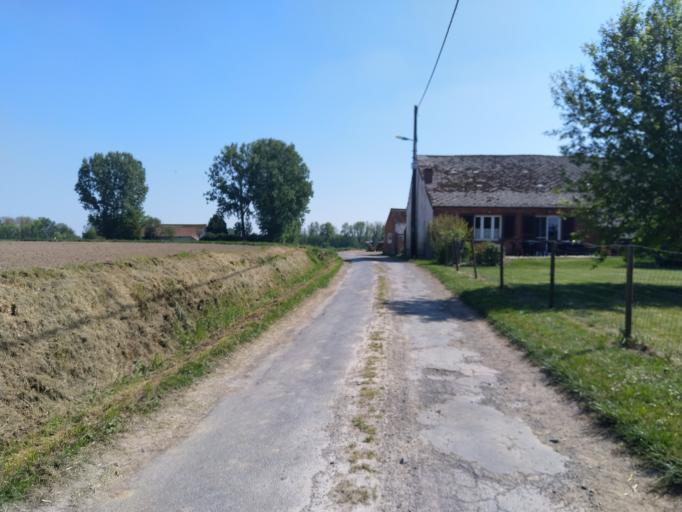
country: BE
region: Wallonia
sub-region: Province du Hainaut
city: Jurbise
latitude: 50.5400
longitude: 3.9862
